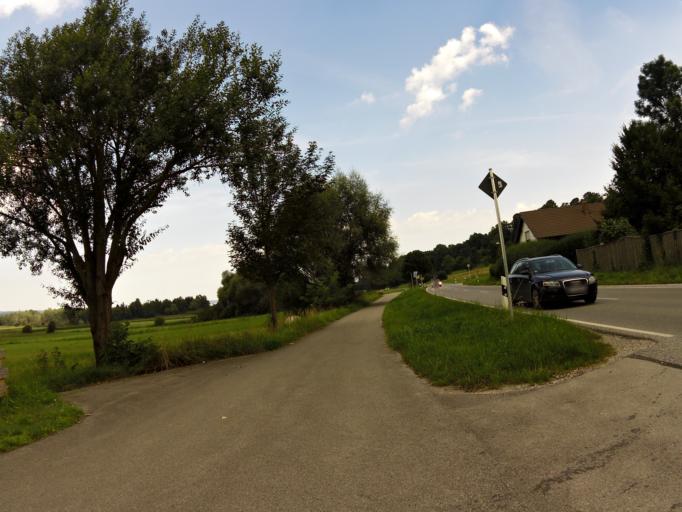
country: DE
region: Bavaria
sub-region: Upper Bavaria
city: Pahl
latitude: 47.9327
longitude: 11.1539
